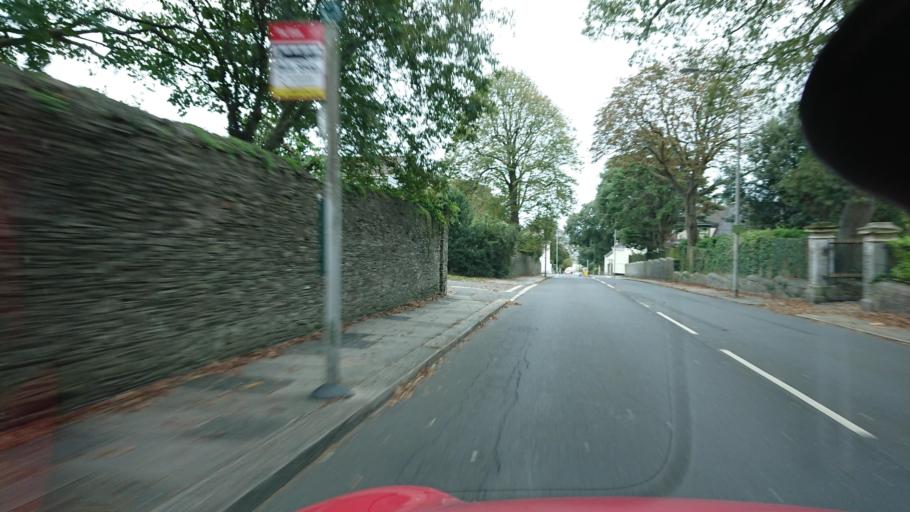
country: GB
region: England
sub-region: Plymouth
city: Plymouth
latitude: 50.3793
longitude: -4.1624
